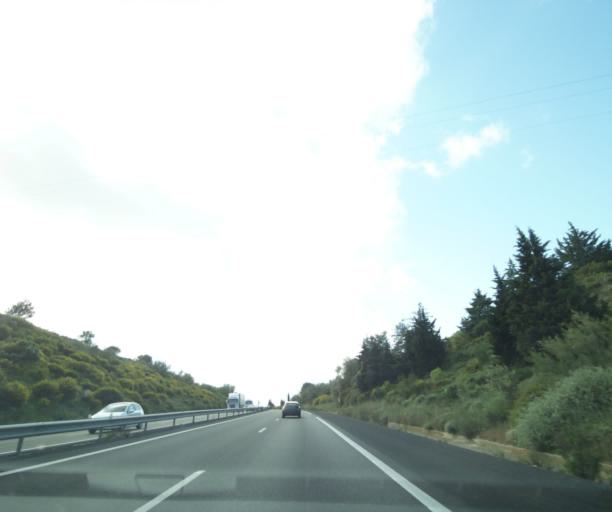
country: FR
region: Languedoc-Roussillon
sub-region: Departement du Gard
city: Garons
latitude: 43.7384
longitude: 4.4601
